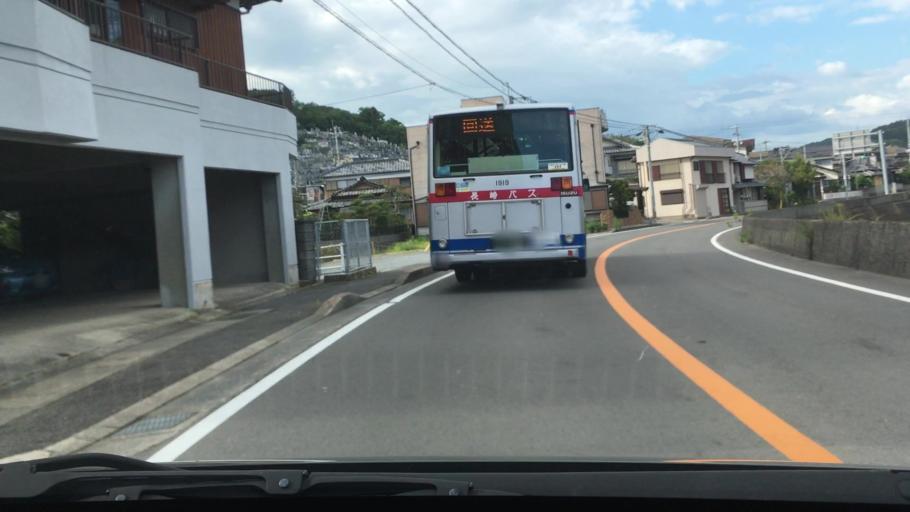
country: JP
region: Nagasaki
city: Togitsu
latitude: 32.8240
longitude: 129.7495
